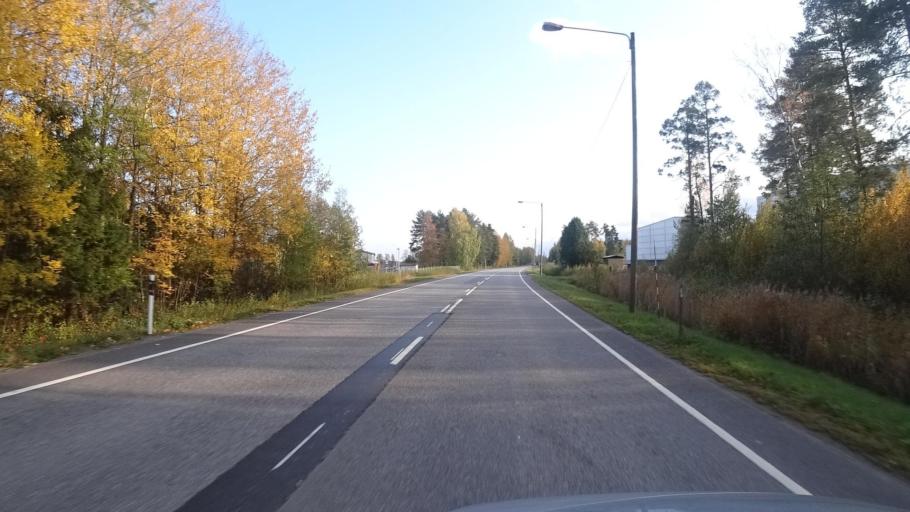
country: FI
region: Satakunta
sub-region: Rauma
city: Saekylae
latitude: 61.0648
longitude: 22.3232
